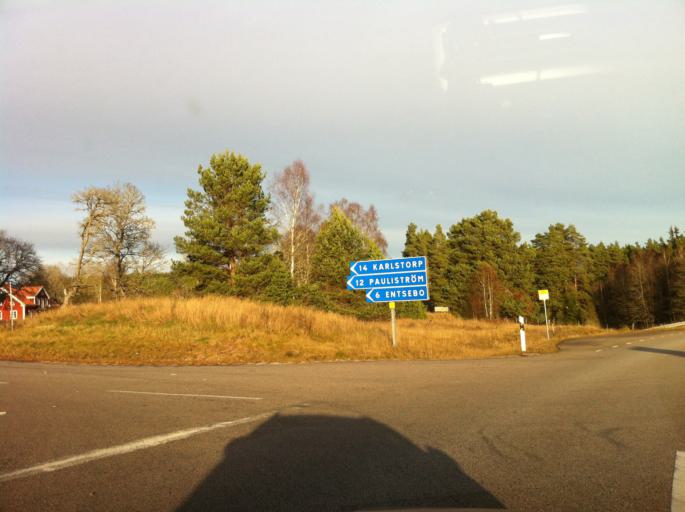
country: SE
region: Kalmar
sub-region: Hultsfreds Kommun
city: Virserum
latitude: 57.4177
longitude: 15.6267
